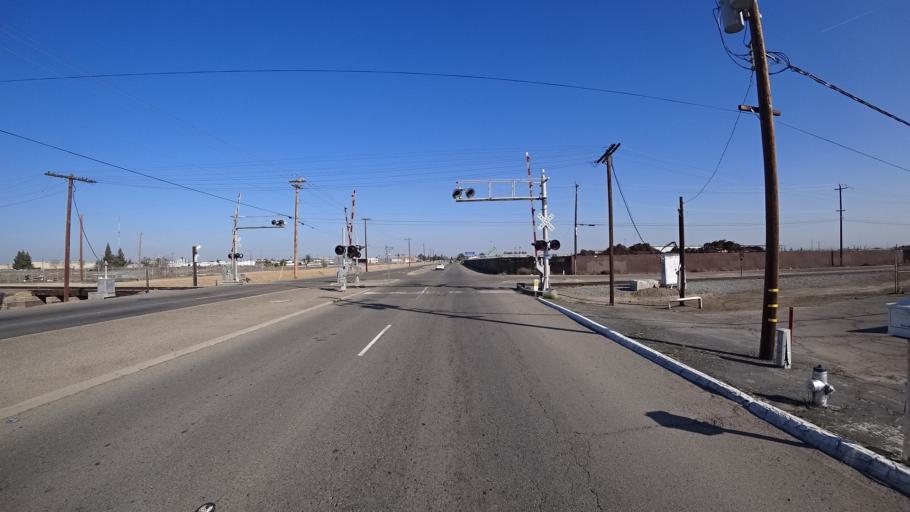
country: US
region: California
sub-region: Fresno County
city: Fresno
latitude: 36.6995
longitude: -119.7364
